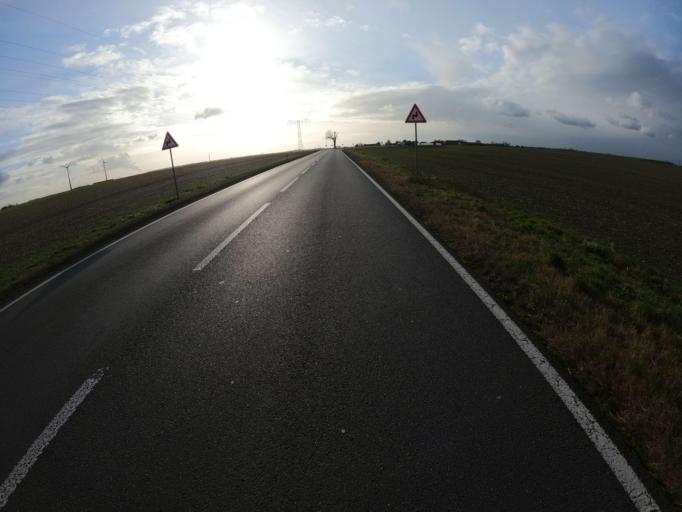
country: DE
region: Saxony-Anhalt
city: Gunthersdorf
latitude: 51.3387
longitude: 12.2082
